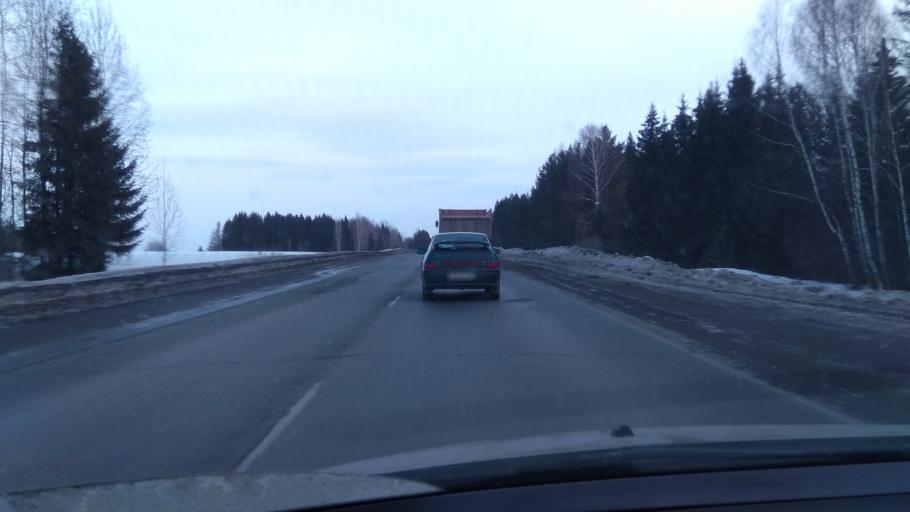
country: RU
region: Perm
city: Kukushtan
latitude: 57.5335
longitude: 56.6094
